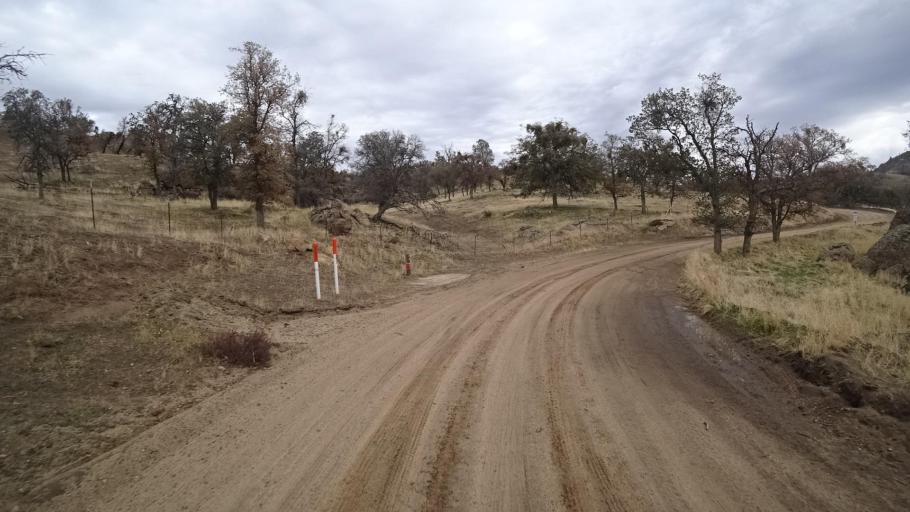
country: US
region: California
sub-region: Kern County
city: Stallion Springs
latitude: 35.1108
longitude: -118.6849
